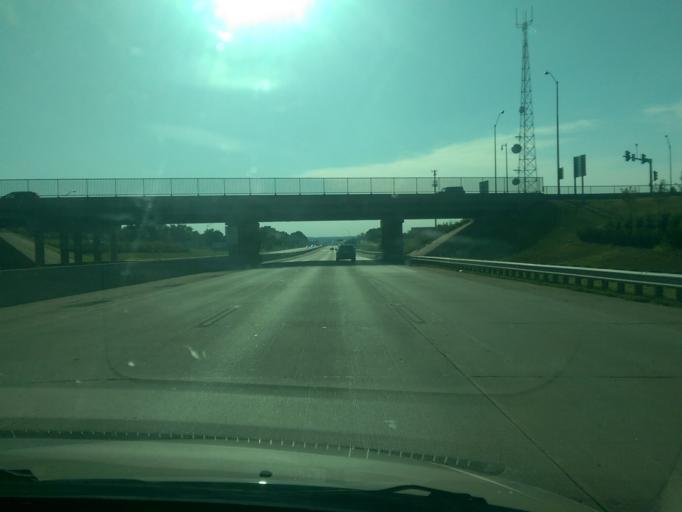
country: US
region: Missouri
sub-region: Jackson County
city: Blue Springs
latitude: 39.0342
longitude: -94.3046
